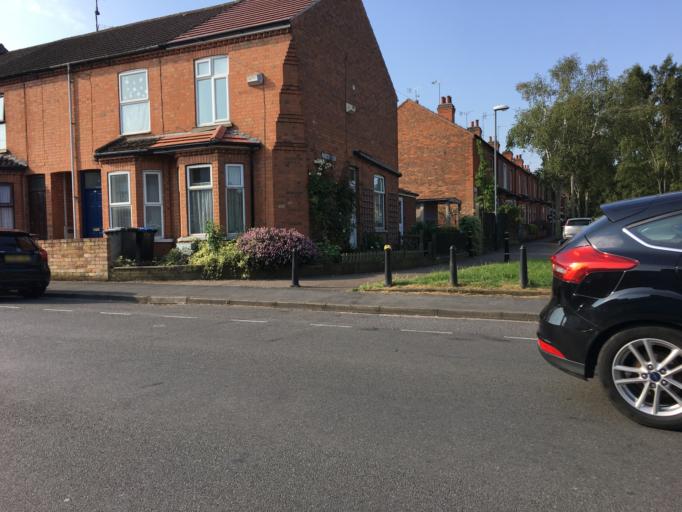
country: GB
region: England
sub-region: Warwickshire
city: Rugby
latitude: 52.3790
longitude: -1.2602
